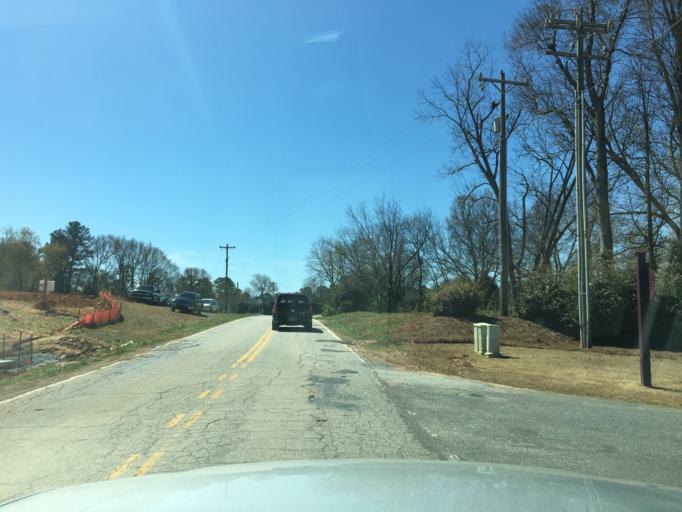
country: US
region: South Carolina
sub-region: Spartanburg County
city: Roebuck
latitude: 34.8940
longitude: -81.9677
